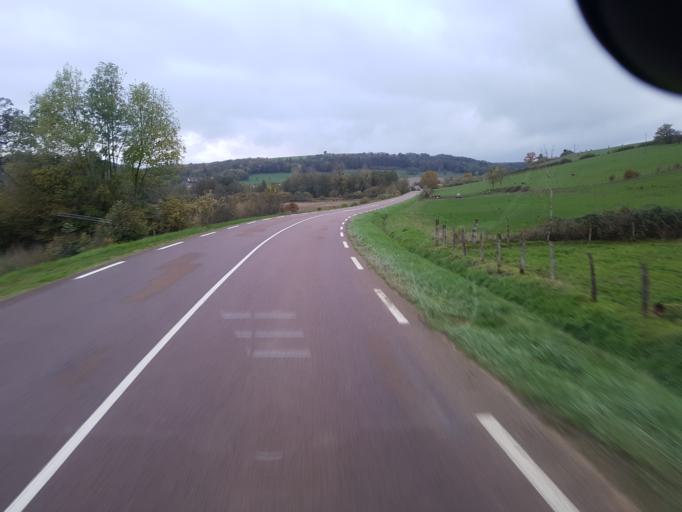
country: FR
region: Bourgogne
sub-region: Departement de la Cote-d'Or
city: Chatillon-sur-Seine
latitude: 47.6764
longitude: 4.6798
